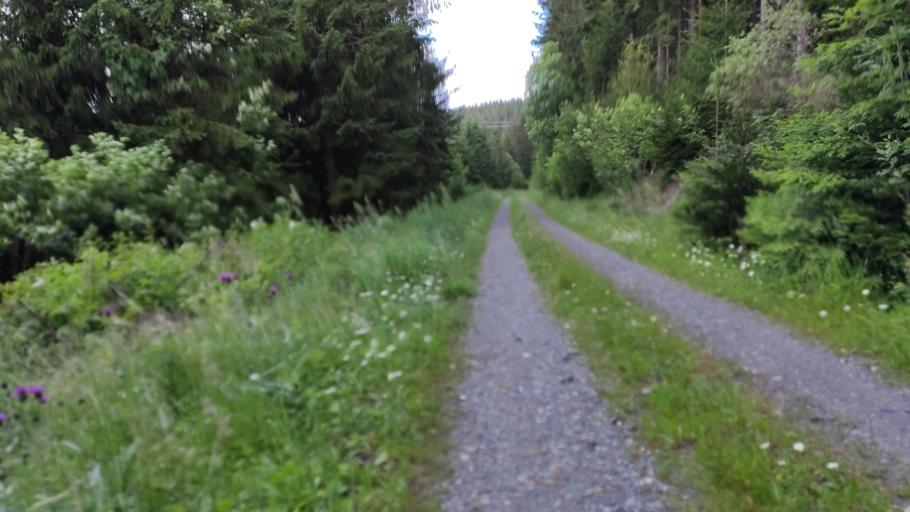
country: DE
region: Bavaria
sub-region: Upper Franconia
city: Tschirn
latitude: 50.4080
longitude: 11.4666
